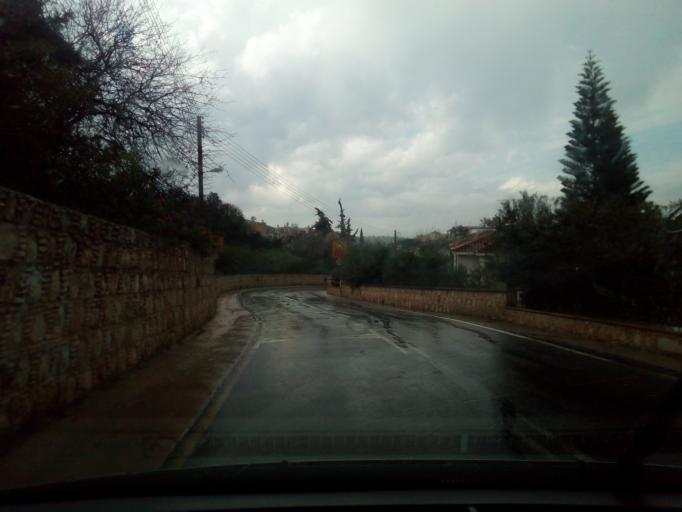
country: CY
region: Pafos
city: Polis
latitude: 34.9958
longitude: 32.4730
